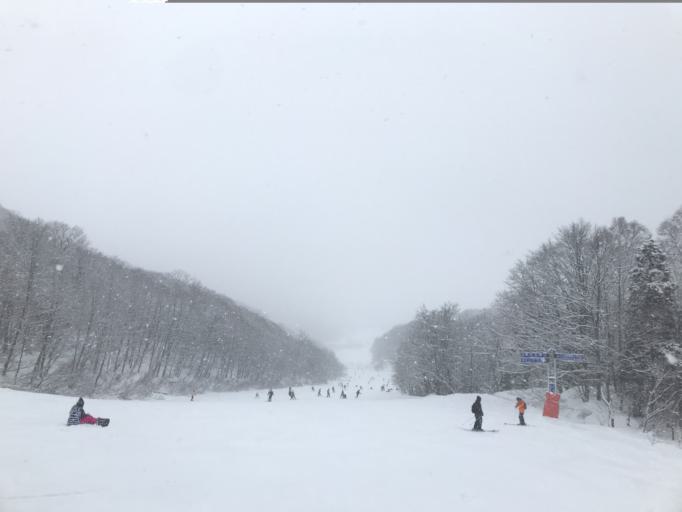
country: JP
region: Nagano
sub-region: Kitaazumi Gun
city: Hakuba
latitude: 36.7550
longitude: 137.8472
